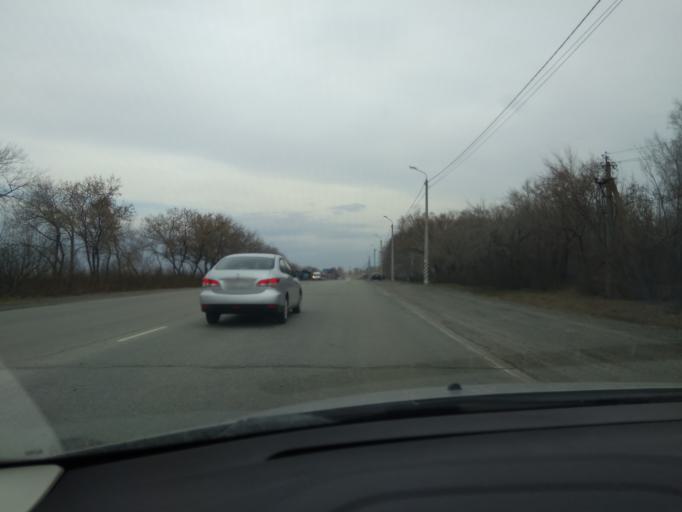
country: RU
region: Chelyabinsk
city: Potanino
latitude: 55.2876
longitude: 61.5104
